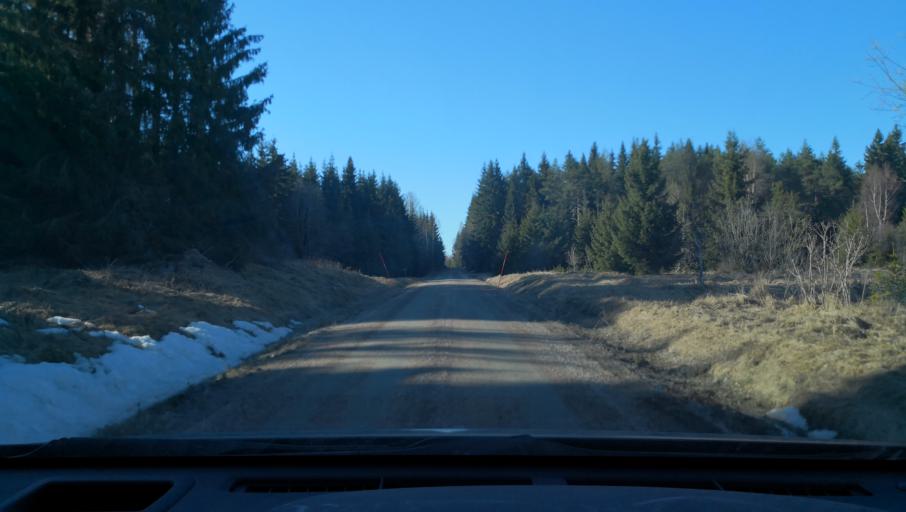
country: SE
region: Vaestmanland
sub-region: Sala Kommun
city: Sala
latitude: 60.1172
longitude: 16.6698
